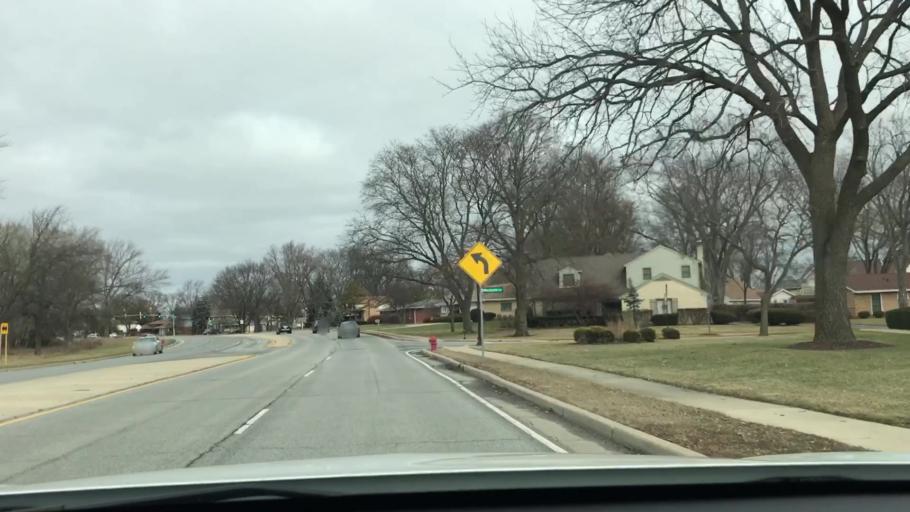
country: US
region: Illinois
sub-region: Cook County
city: Elk Grove Village
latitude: 42.0198
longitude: -87.9894
